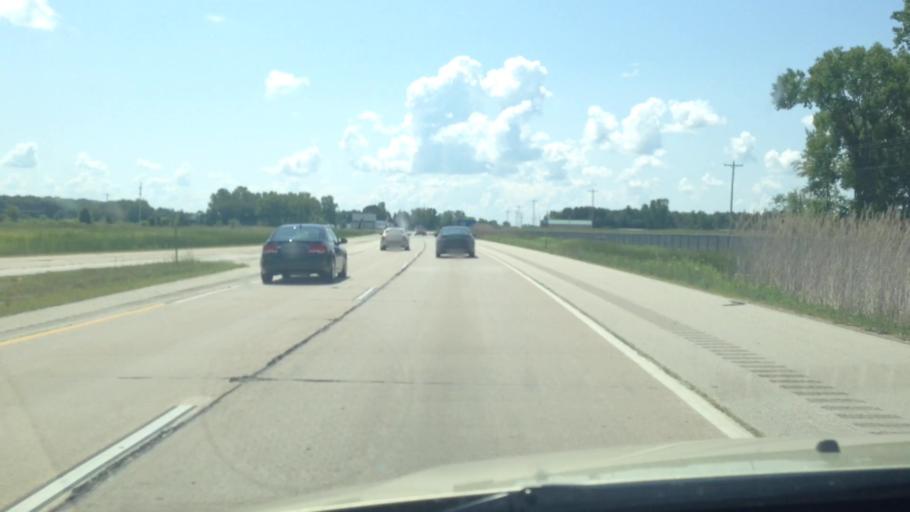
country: US
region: Wisconsin
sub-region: Brown County
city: Suamico
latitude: 44.7406
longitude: -88.0521
